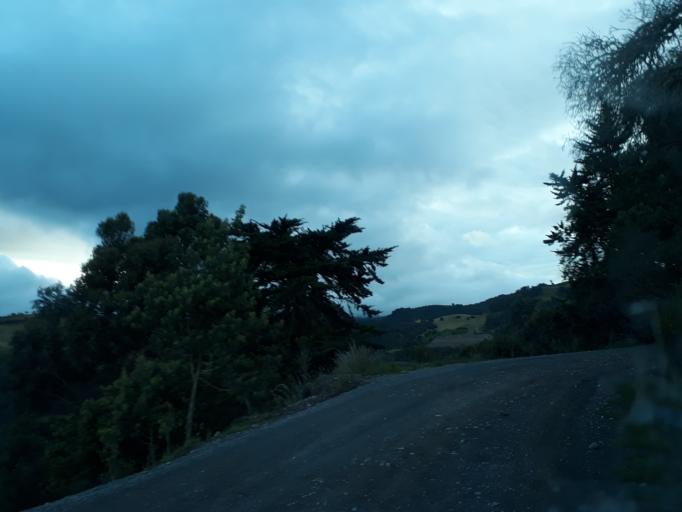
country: CO
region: Cundinamarca
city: Carmen de Carupa
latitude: 5.3438
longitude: -73.9068
